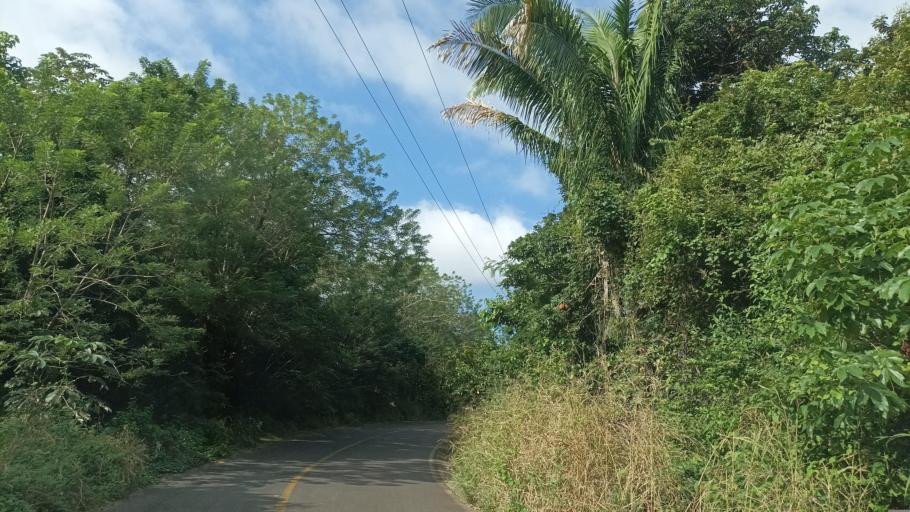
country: MX
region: Veracruz
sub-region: Pajapan
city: Pajapan
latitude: 18.1860
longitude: -94.6813
